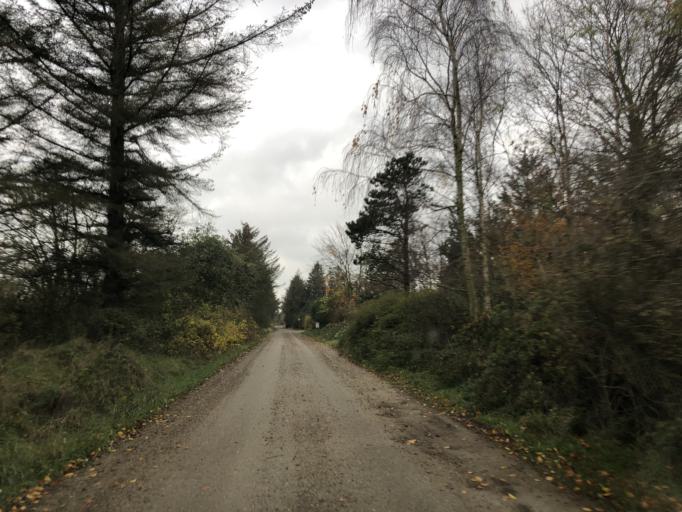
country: DK
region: Central Jutland
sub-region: Holstebro Kommune
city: Ulfborg
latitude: 56.3147
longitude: 8.2143
